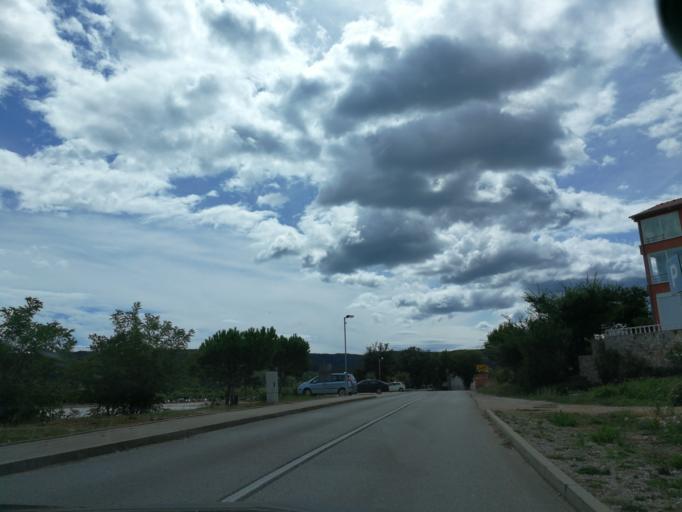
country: HR
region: Primorsko-Goranska
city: Njivice
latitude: 45.1552
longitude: 14.5977
